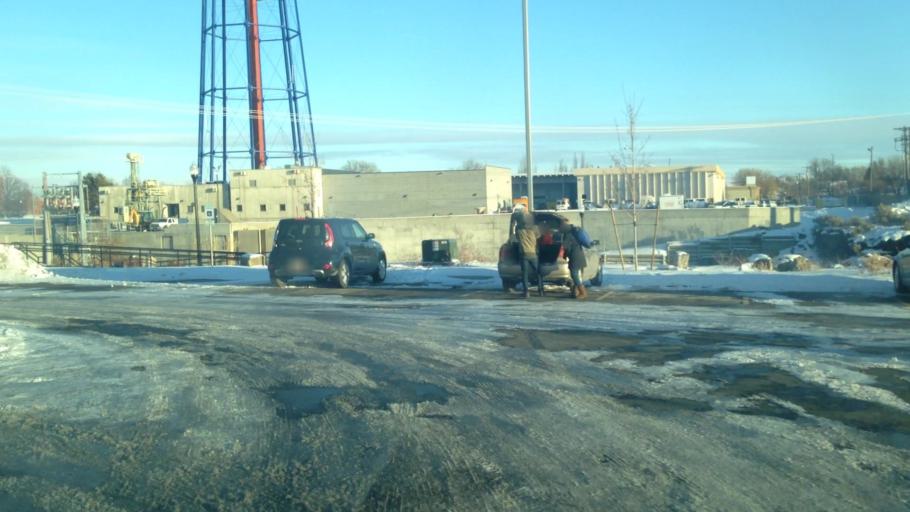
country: US
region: Idaho
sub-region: Bonneville County
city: Idaho Falls
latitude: 43.4913
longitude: -112.0469
